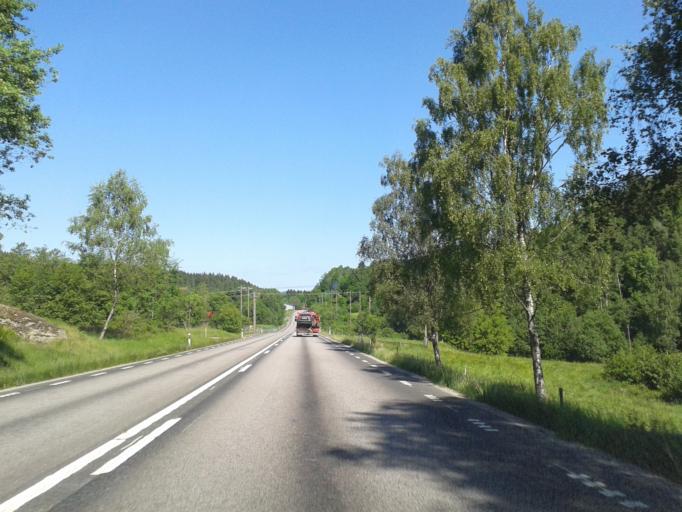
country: SE
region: Vaestra Goetaland
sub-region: Orust
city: Henan
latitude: 58.2169
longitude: 11.6903
